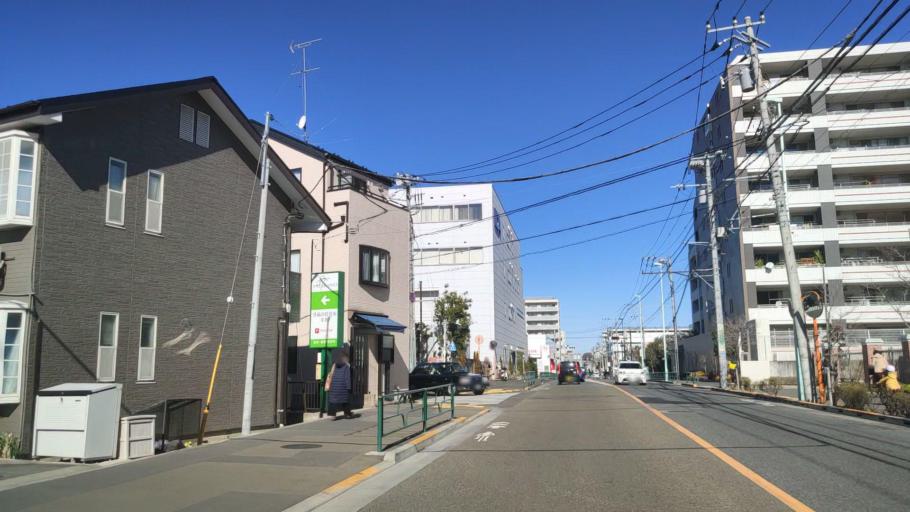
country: JP
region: Tokyo
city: Mitaka-shi
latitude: 35.6856
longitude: 139.5686
